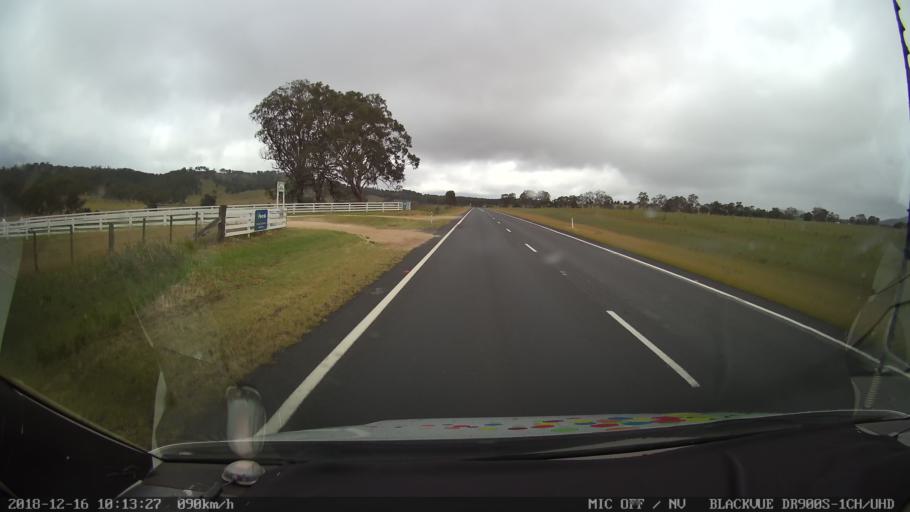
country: AU
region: New South Wales
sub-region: Glen Innes Severn
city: Glen Innes
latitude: -29.2971
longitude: 151.9527
